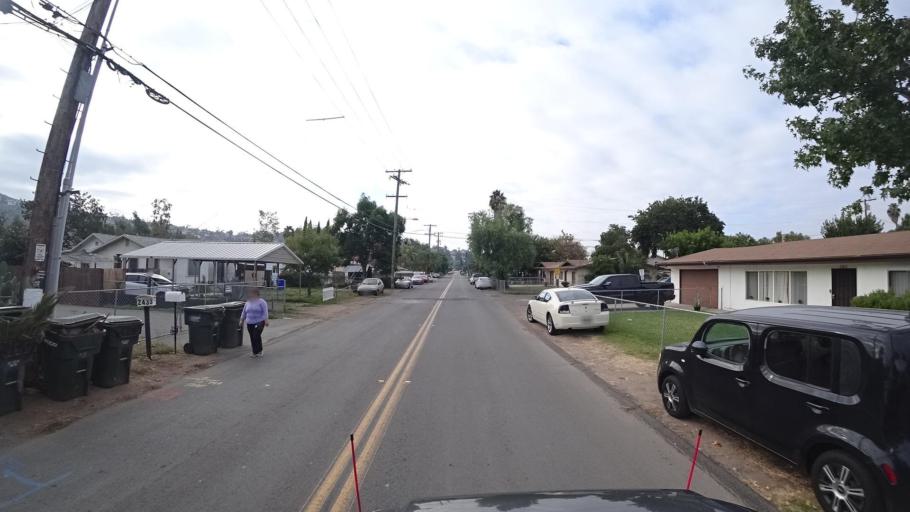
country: US
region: California
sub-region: San Diego County
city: Spring Valley
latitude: 32.7321
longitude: -117.0101
